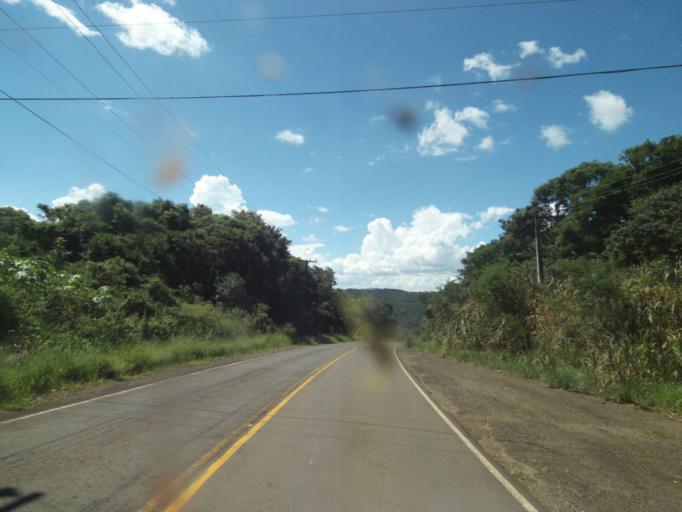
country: BR
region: Parana
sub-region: Chopinzinho
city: Chopinzinho
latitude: -25.7833
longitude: -52.1013
